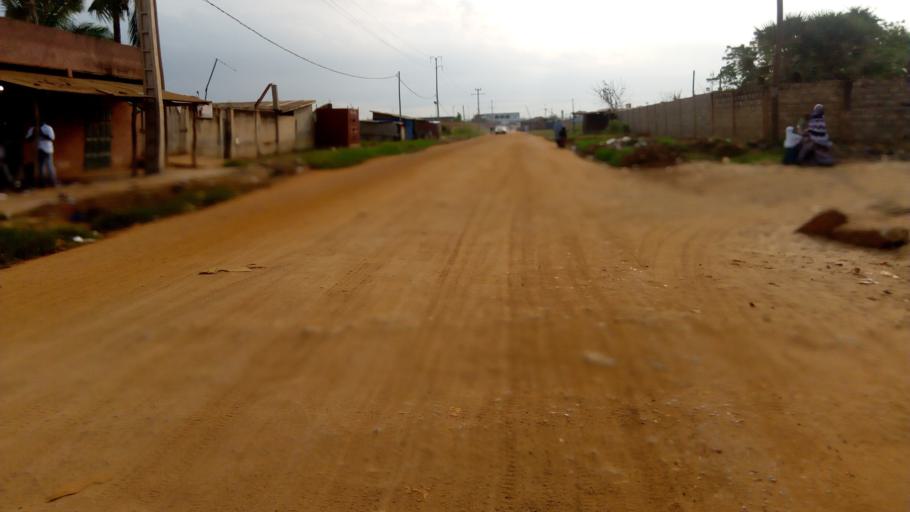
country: TG
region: Maritime
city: Lome
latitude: 6.2518
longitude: 1.2117
